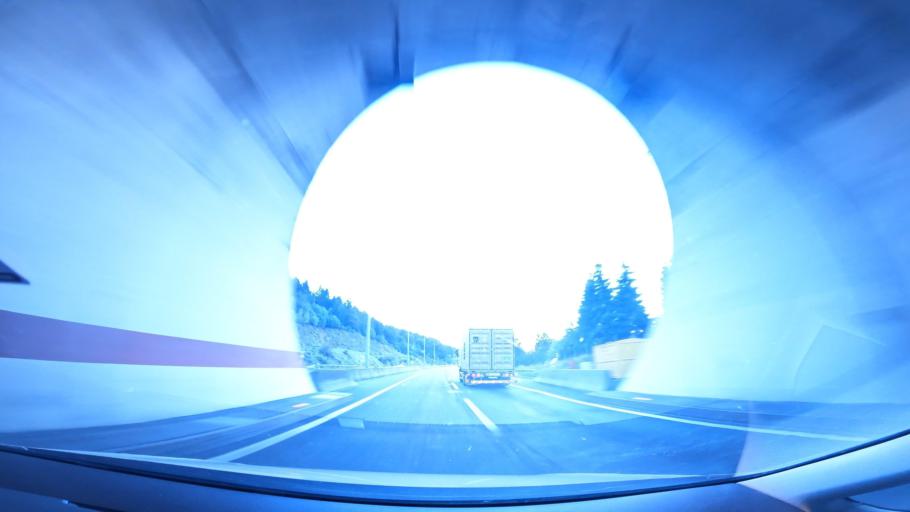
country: HR
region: Primorsko-Goranska
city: Vrbovsko
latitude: 45.3756
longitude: 15.0073
